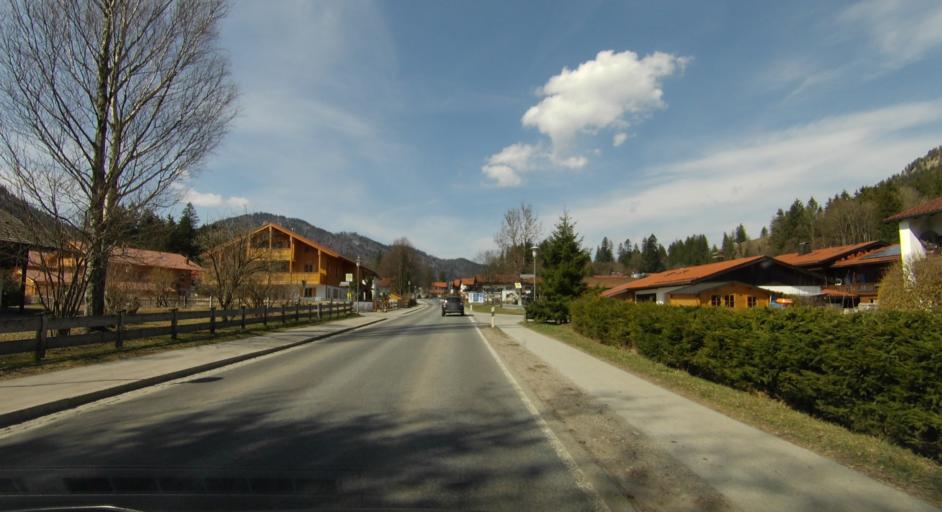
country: DE
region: Bavaria
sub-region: Upper Bavaria
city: Schliersee
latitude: 47.7020
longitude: 11.8865
